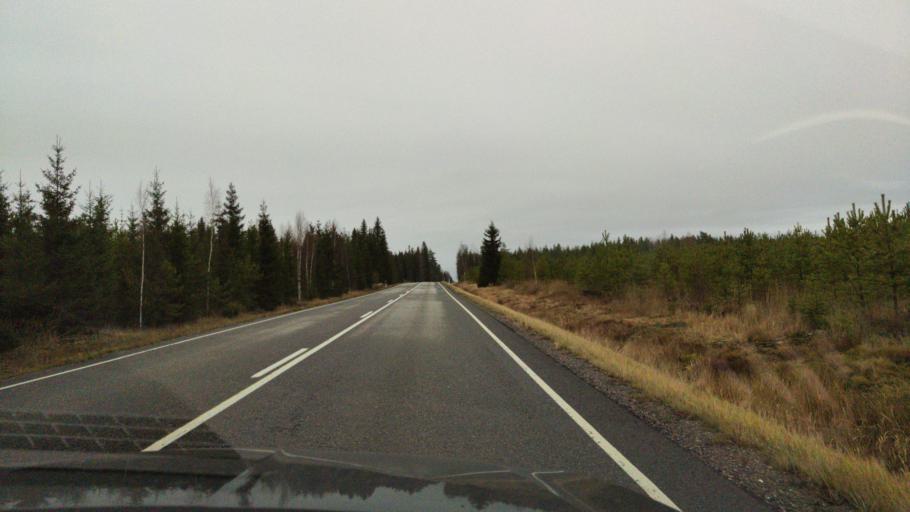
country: FI
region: Varsinais-Suomi
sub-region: Loimaa
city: Ylaene
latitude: 60.7610
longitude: 22.4317
